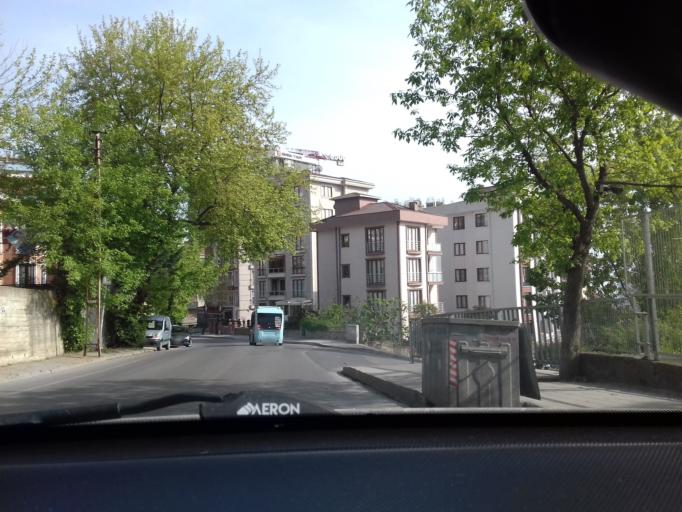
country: TR
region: Istanbul
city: Pendik
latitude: 40.9107
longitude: 29.2336
